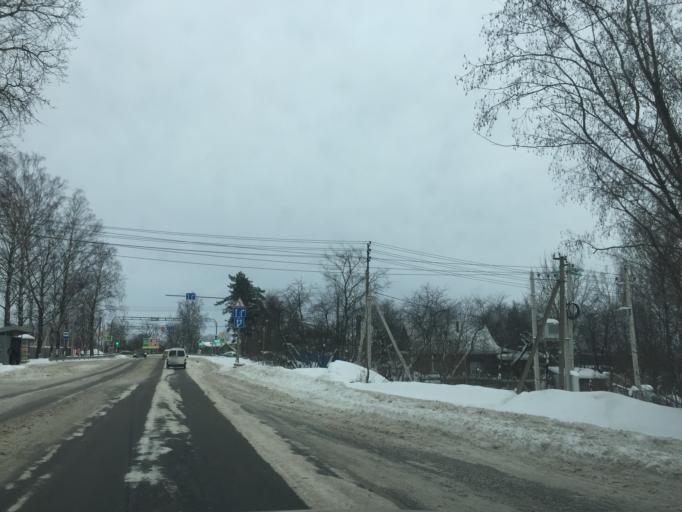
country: RU
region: Leningrad
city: Yanino Vtoroye
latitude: 59.9294
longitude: 30.6193
